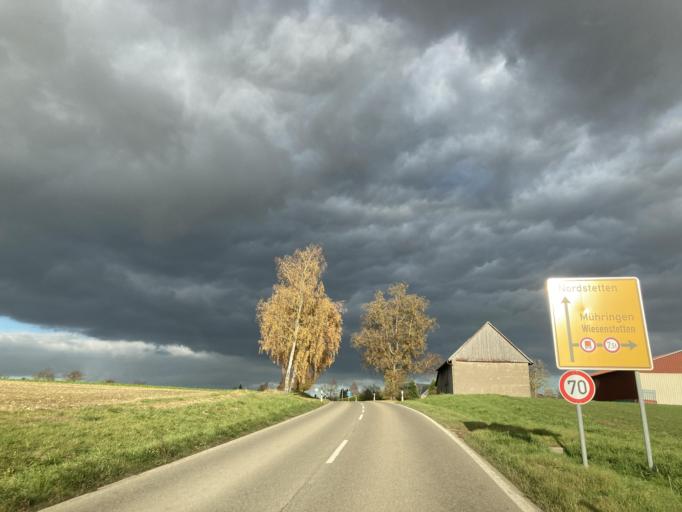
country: DE
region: Baden-Wuerttemberg
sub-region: Karlsruhe Region
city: Empfingen
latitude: 48.3967
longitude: 8.7418
